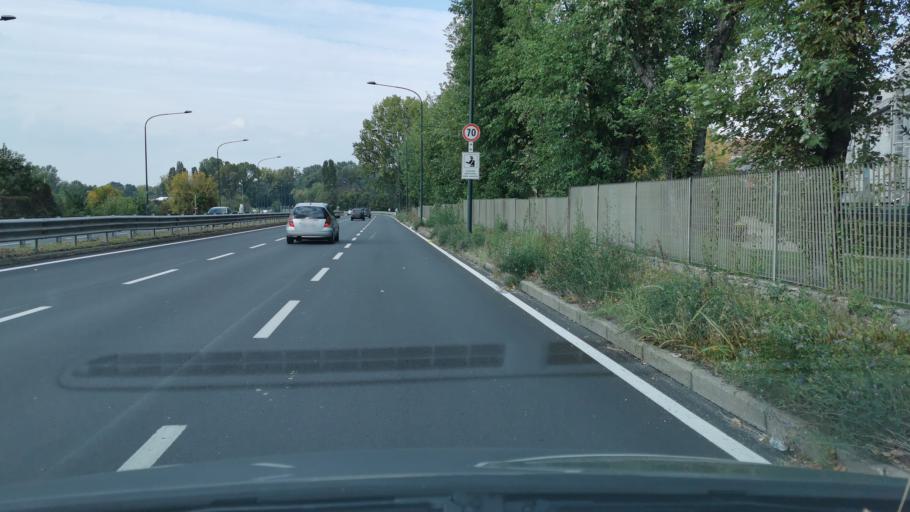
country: IT
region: Piedmont
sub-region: Provincia di Torino
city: San Mauro Torinese
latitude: 45.0842
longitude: 7.7290
